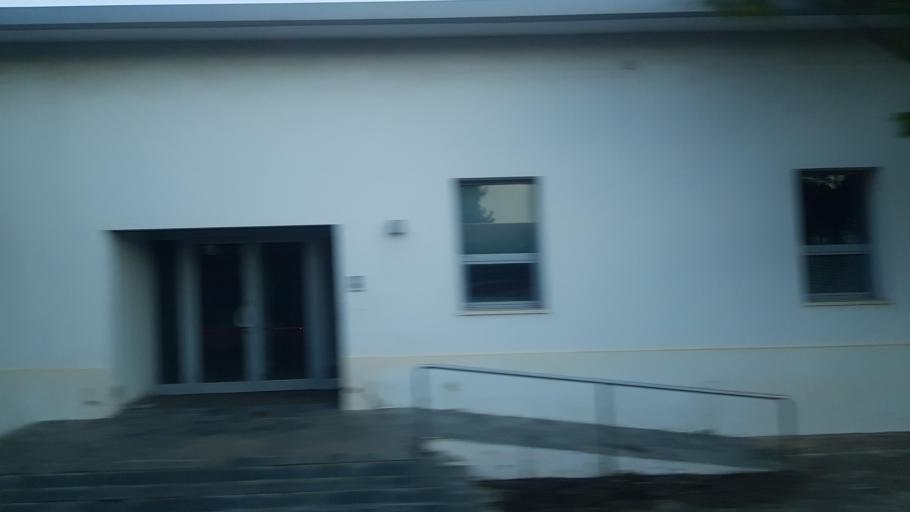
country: ES
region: Valencia
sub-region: Provincia de Valencia
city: Manises
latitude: 39.4789
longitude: -0.4845
